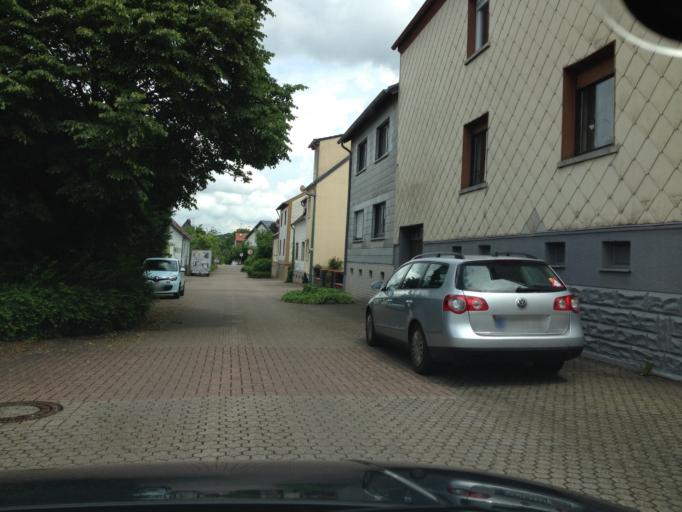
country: DE
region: Saarland
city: Bexbach
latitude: 49.3093
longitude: 7.2793
